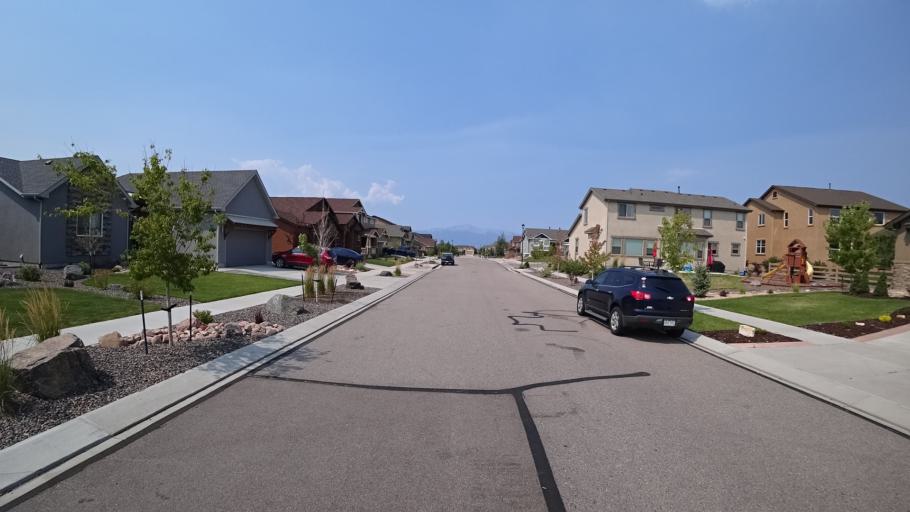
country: US
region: Colorado
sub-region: El Paso County
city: Black Forest
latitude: 38.9634
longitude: -104.7180
